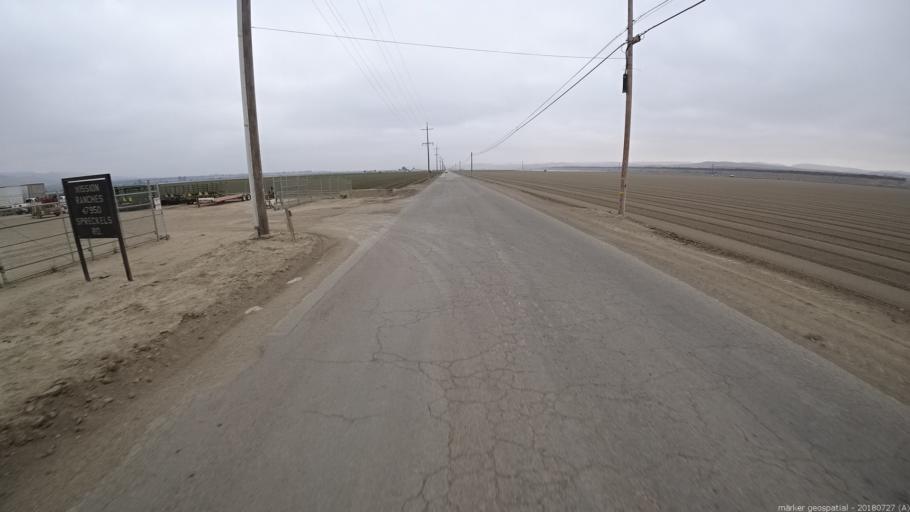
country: US
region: California
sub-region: Monterey County
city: King City
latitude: 36.2301
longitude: -121.1409
